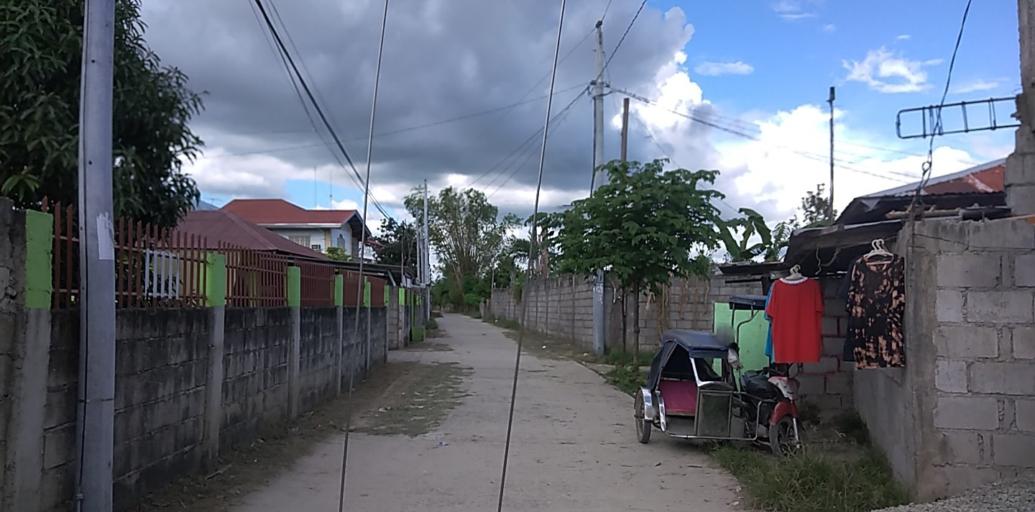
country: PH
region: Central Luzon
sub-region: Province of Pampanga
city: Arayat
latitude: 15.1355
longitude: 120.7823
